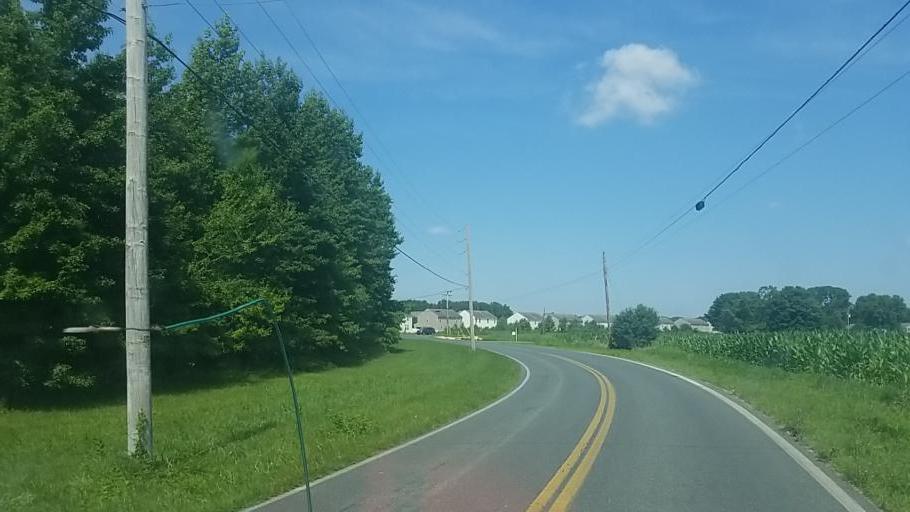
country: US
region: Maryland
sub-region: Caroline County
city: Denton
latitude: 38.8835
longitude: -75.7991
